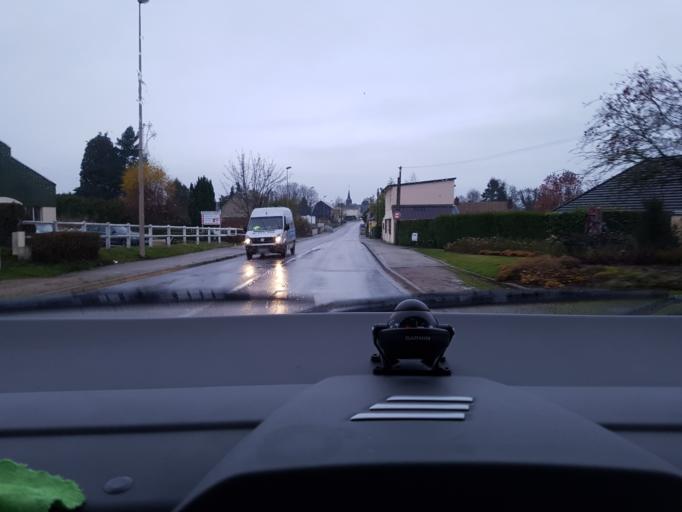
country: FR
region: Haute-Normandie
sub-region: Departement de l'Eure
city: Saint-Pierre-des-Fleurs
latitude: 49.2482
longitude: 0.9636
